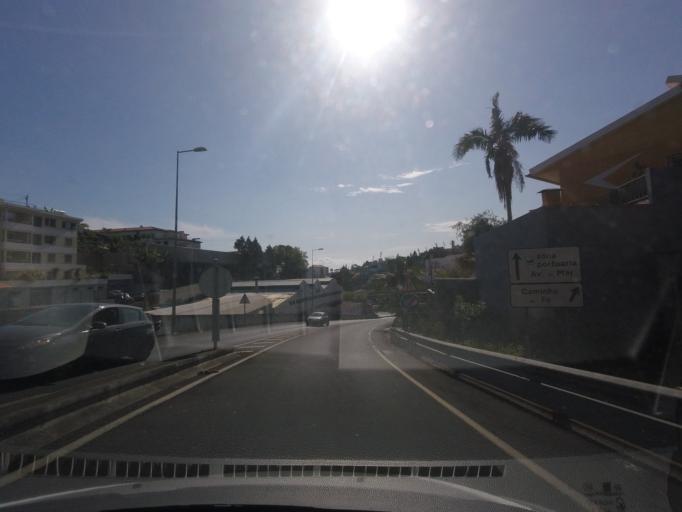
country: PT
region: Madeira
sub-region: Funchal
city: Nossa Senhora do Monte
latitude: 32.6510
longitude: -16.9265
